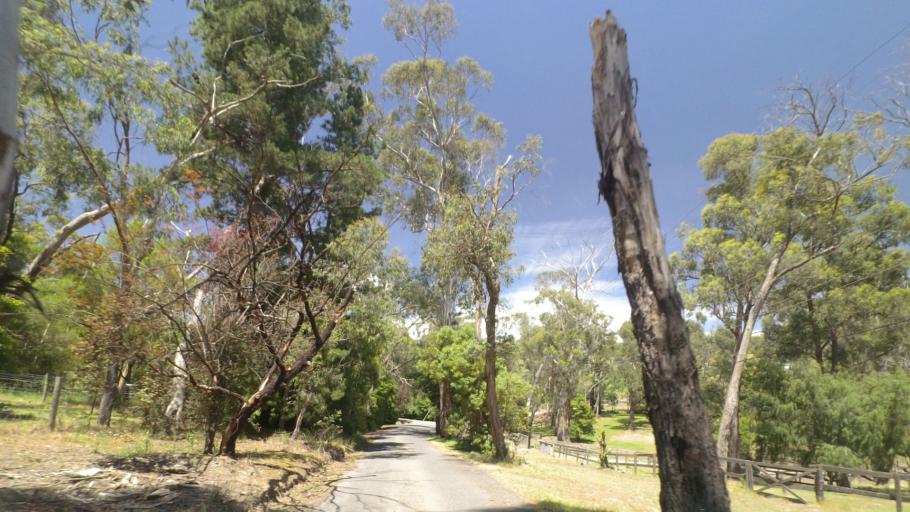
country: AU
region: Victoria
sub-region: Yarra Ranges
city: Chirnside Park
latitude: -37.7503
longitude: 145.2855
